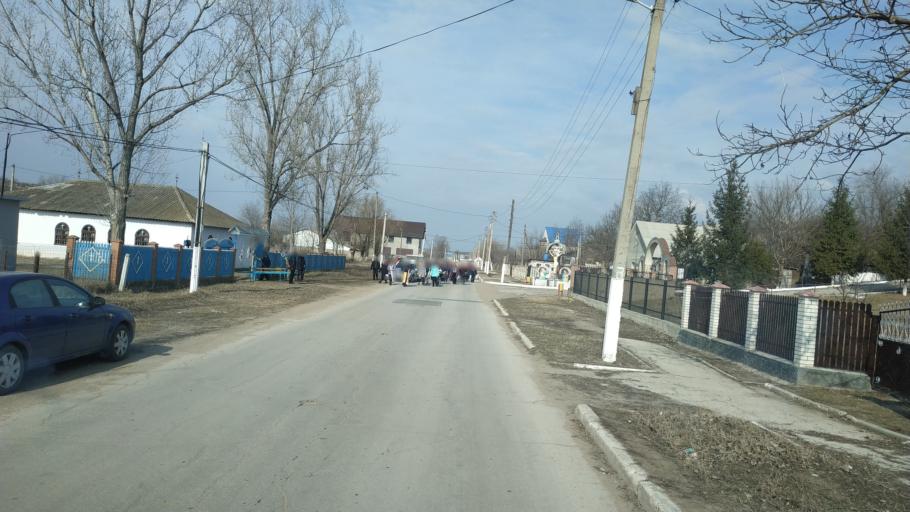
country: MD
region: Anenii Noi
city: Anenii Noi
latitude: 46.9220
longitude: 29.1069
